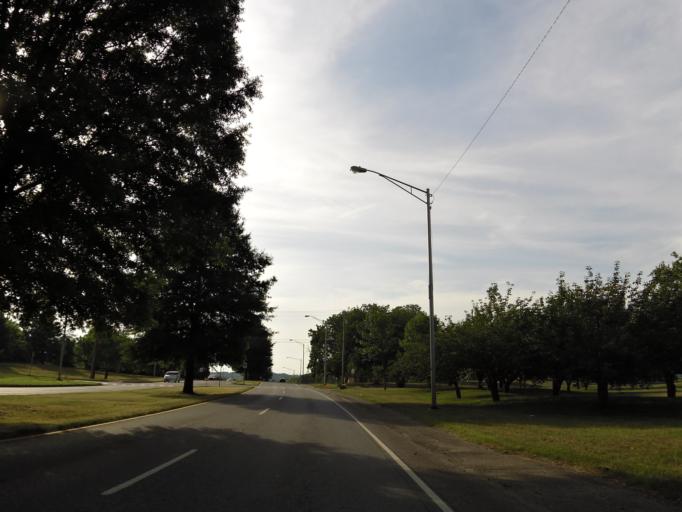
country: US
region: Tennessee
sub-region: Blount County
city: Alcoa
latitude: 35.7785
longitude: -83.9803
